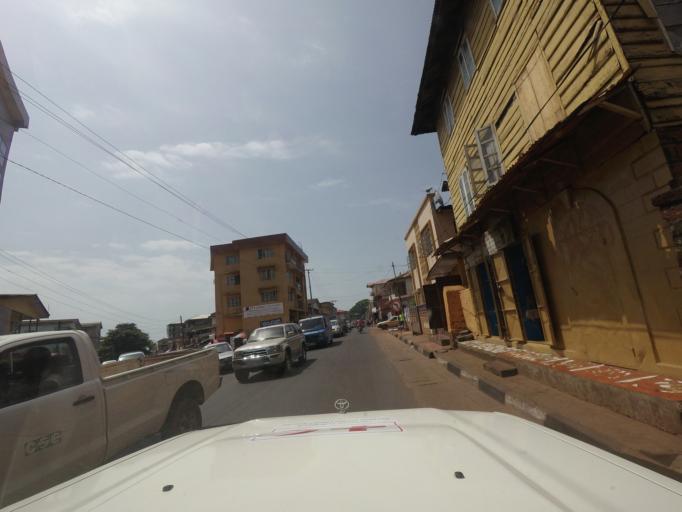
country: SL
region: Western Area
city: Freetown
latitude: 8.4831
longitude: -13.2359
